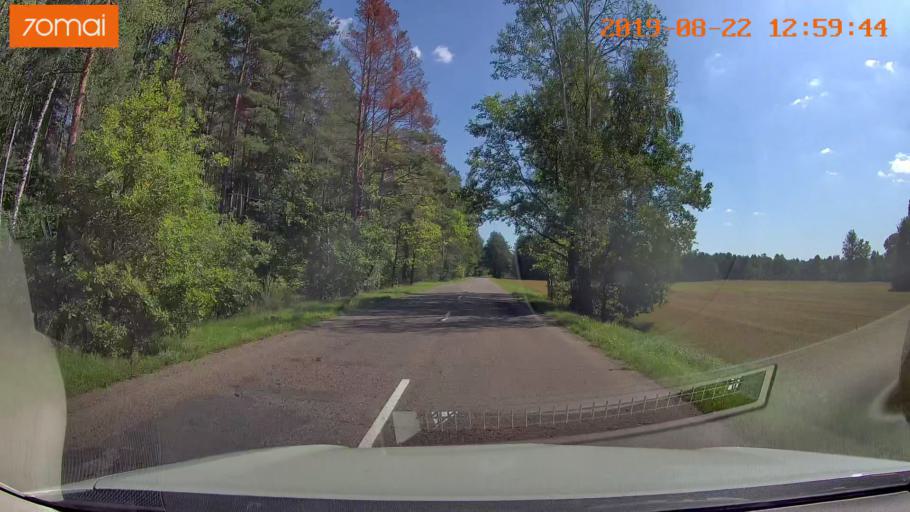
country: BY
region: Minsk
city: Prawdzinski
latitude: 53.4222
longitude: 27.7972
